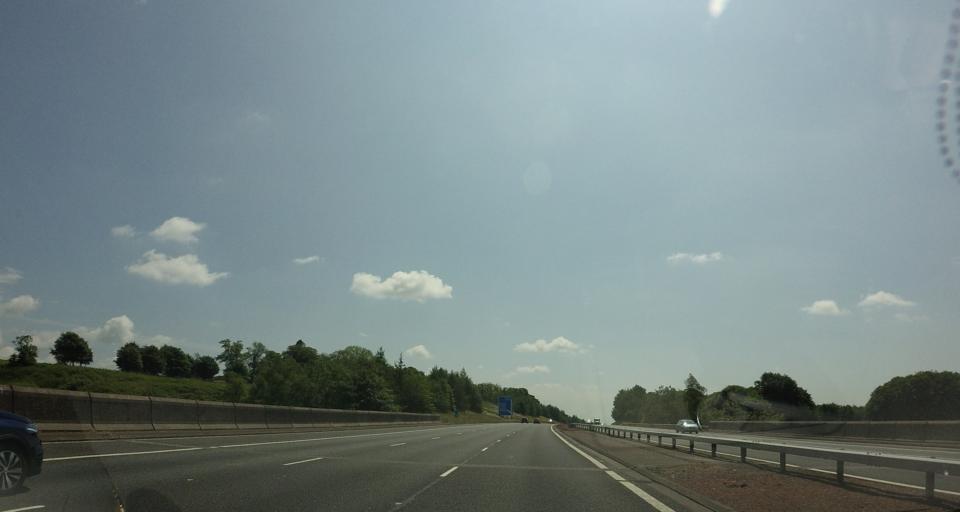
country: GB
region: Scotland
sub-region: Dumfries and Galloway
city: Lockerbie
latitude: 55.1403
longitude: -3.3725
